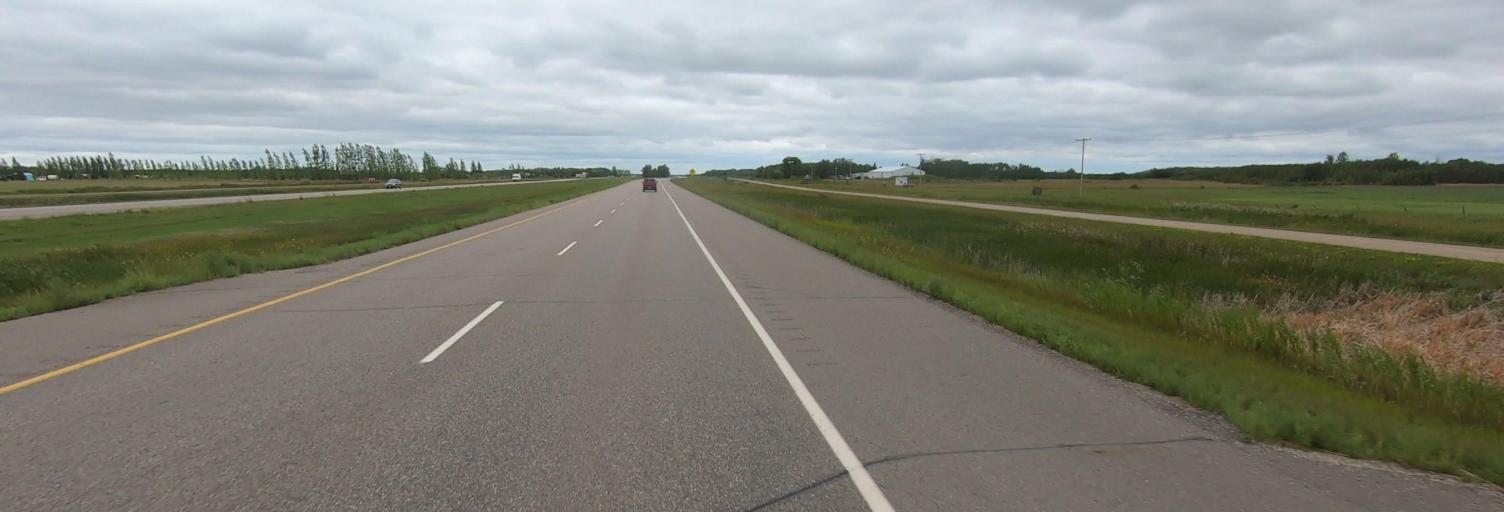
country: CA
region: Manitoba
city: Portage la Prairie
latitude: 49.9752
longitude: -98.6523
